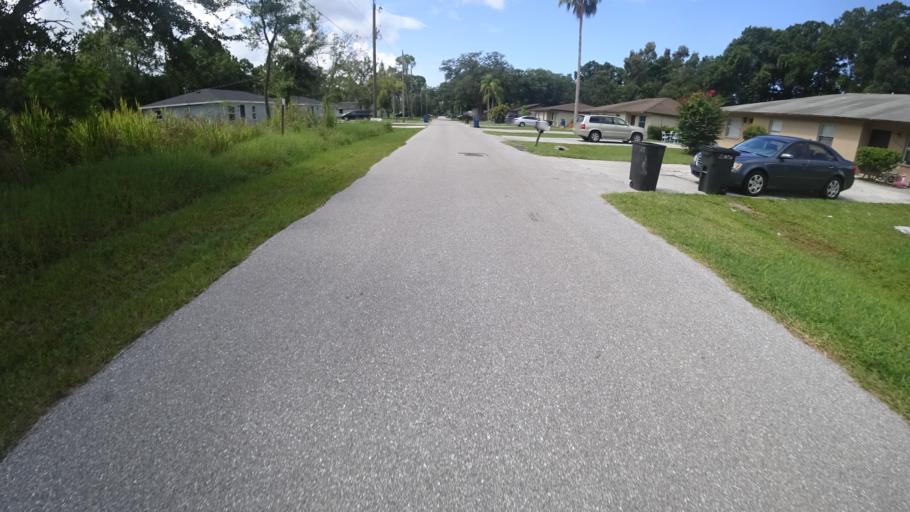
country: US
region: Florida
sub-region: Manatee County
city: Samoset
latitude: 27.4546
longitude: -82.5389
